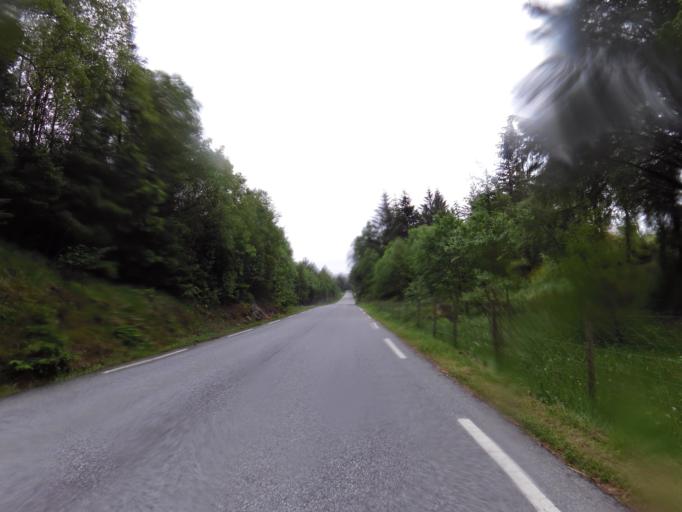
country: NO
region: Hordaland
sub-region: Sveio
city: Sveio
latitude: 59.5230
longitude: 5.2816
